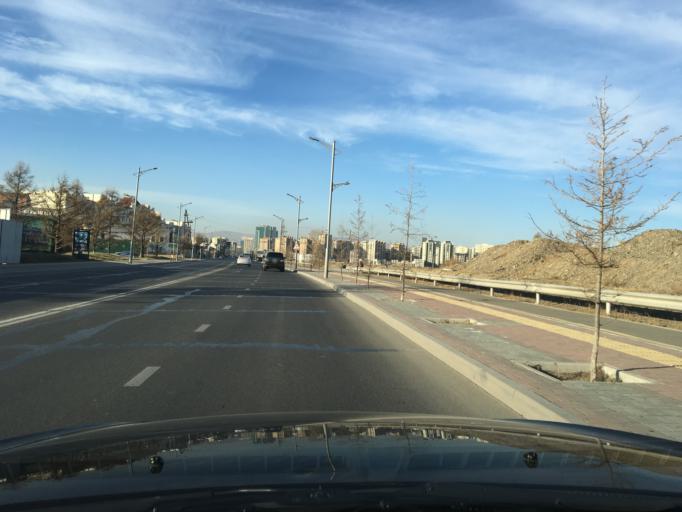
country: MN
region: Ulaanbaatar
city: Ulaanbaatar
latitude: 47.8912
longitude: 106.9382
